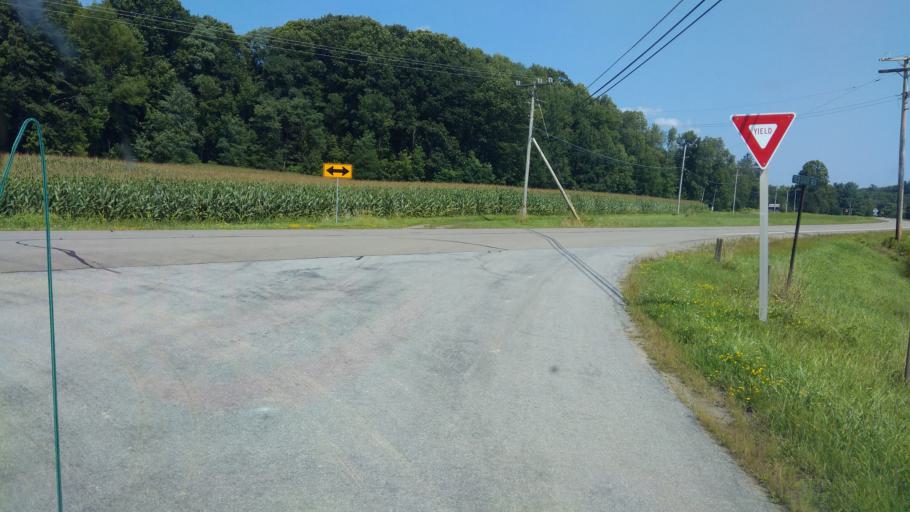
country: US
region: New York
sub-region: Allegany County
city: Belmont
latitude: 42.3045
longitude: -78.0481
